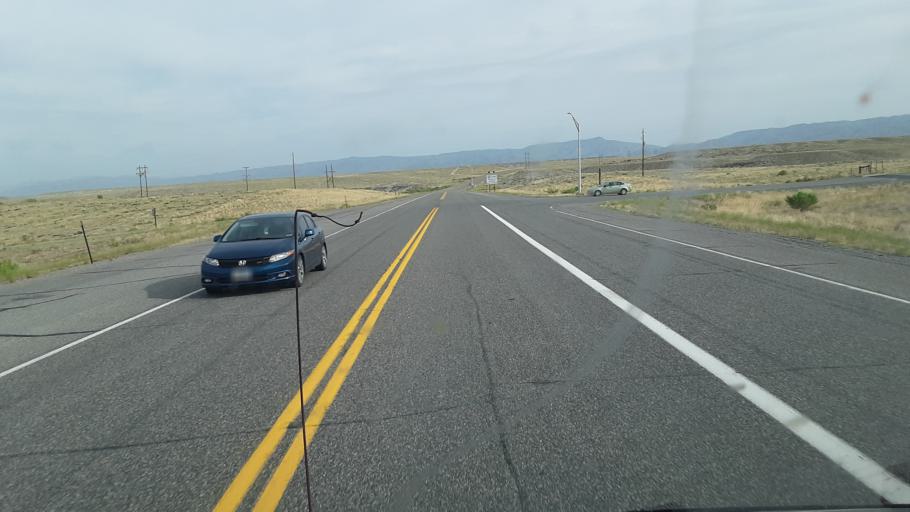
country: US
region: Wyoming
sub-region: Fremont County
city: Riverton
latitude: 43.2806
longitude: -108.1235
